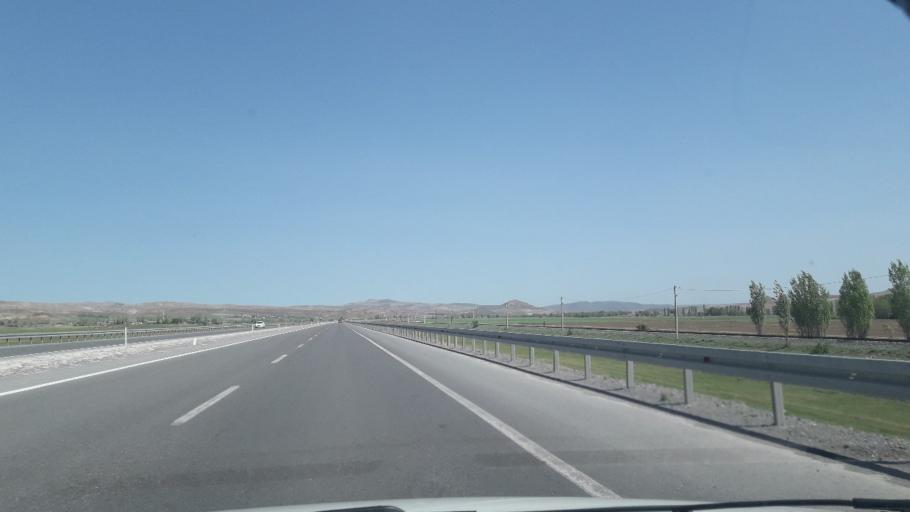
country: TR
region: Sivas
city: Ulas
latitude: 39.4818
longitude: 37.0114
